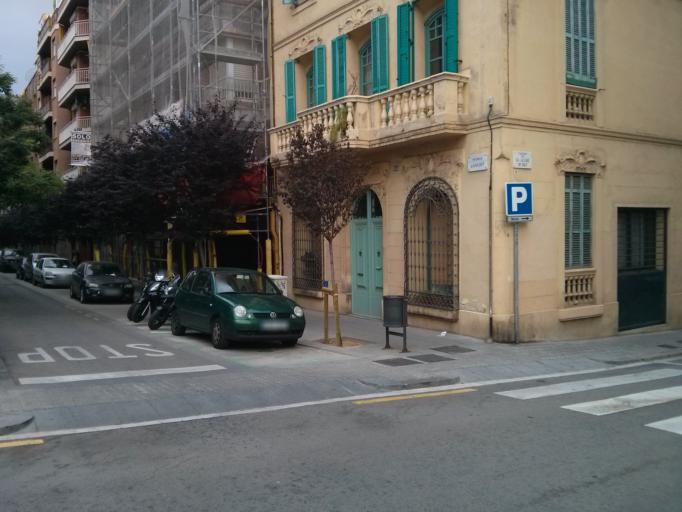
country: ES
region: Catalonia
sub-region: Provincia de Barcelona
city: Gracia
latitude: 41.4102
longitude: 2.1602
